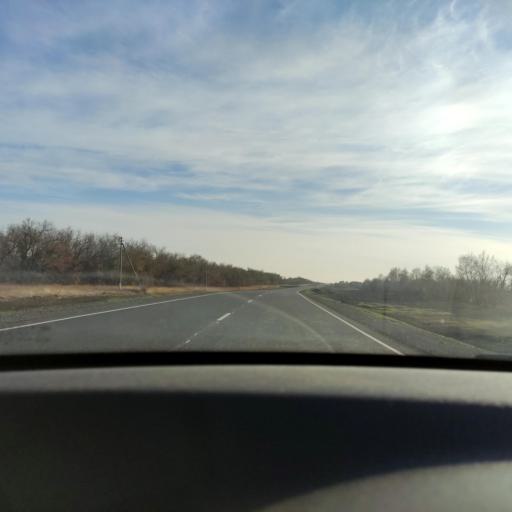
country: RU
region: Samara
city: Krasnoarmeyskoye
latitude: 52.8335
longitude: 50.0059
